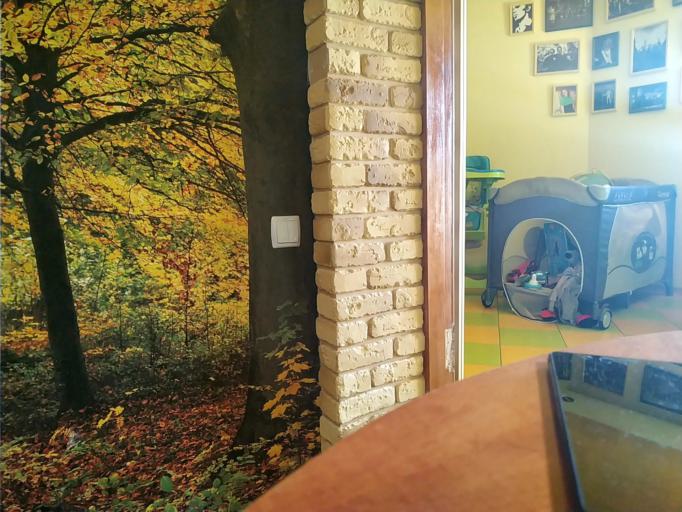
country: RU
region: Tverskaya
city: Vyshniy Volochek
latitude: 57.6061
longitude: 34.5002
